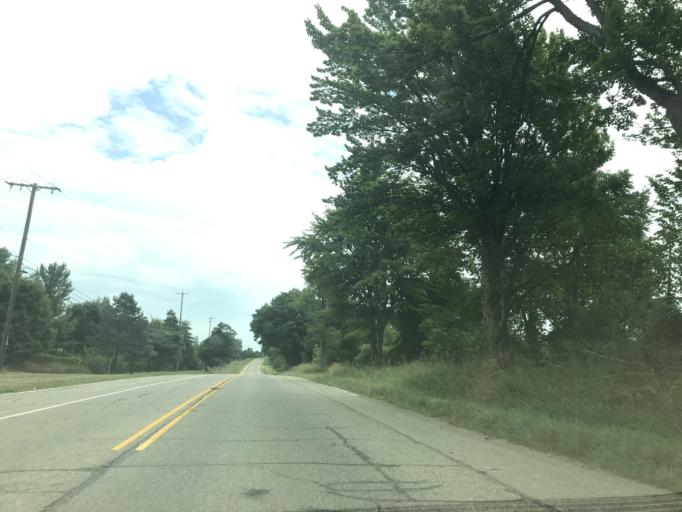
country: US
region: Michigan
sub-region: Clinton County
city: Wacousta
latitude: 42.7899
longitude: -84.6953
